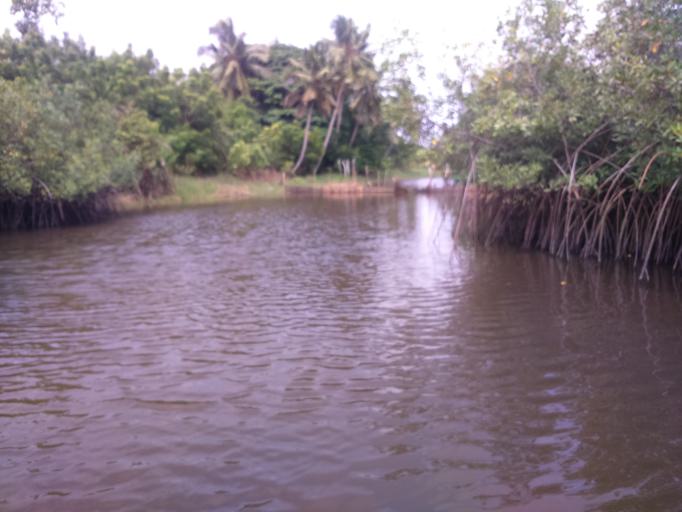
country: BJ
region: Mono
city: Come
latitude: 6.3208
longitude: 1.9142
